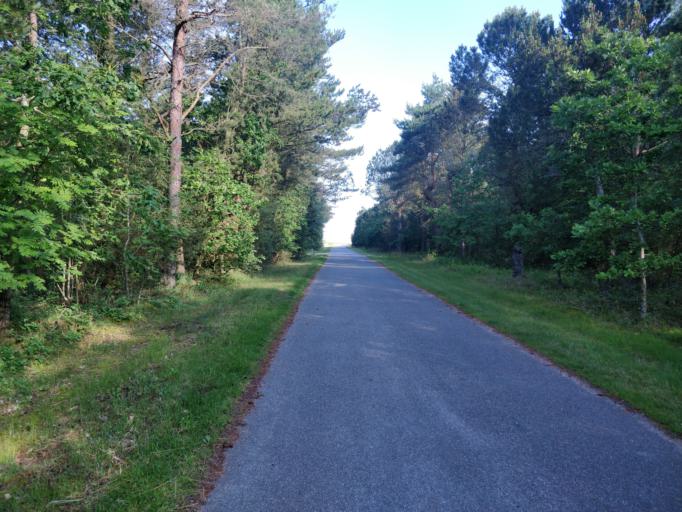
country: DK
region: North Denmark
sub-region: Laeso Kommune
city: Byrum
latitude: 57.2757
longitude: 10.9121
